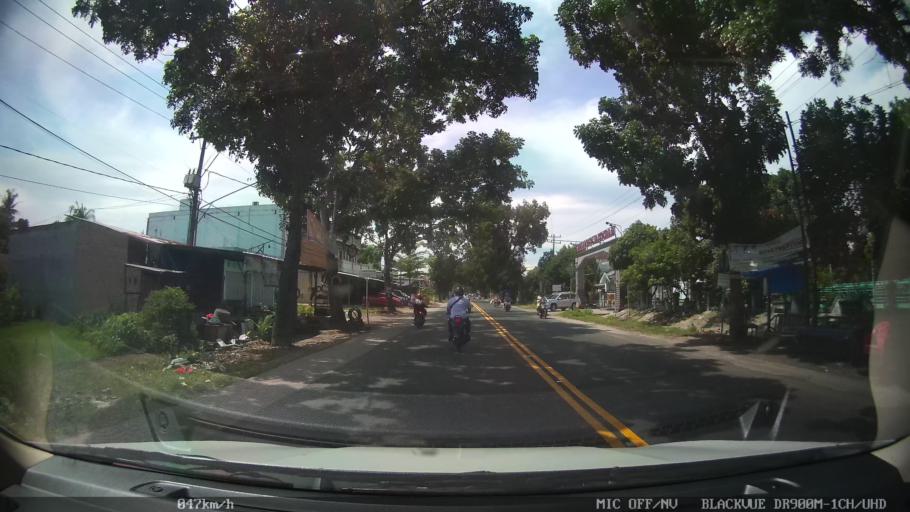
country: ID
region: North Sumatra
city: Binjai
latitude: 3.6487
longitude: 98.5102
